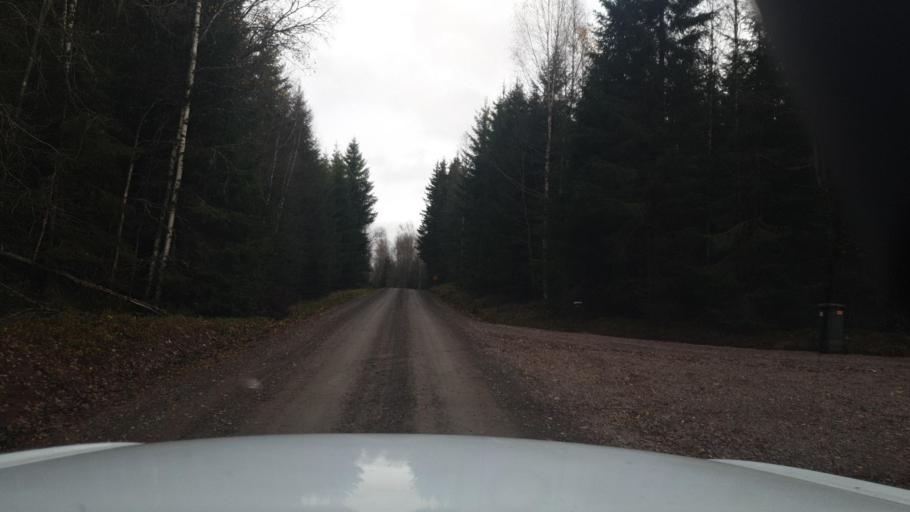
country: SE
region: Vaermland
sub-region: Torsby Kommun
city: Torsby
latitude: 59.9832
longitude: 12.8324
